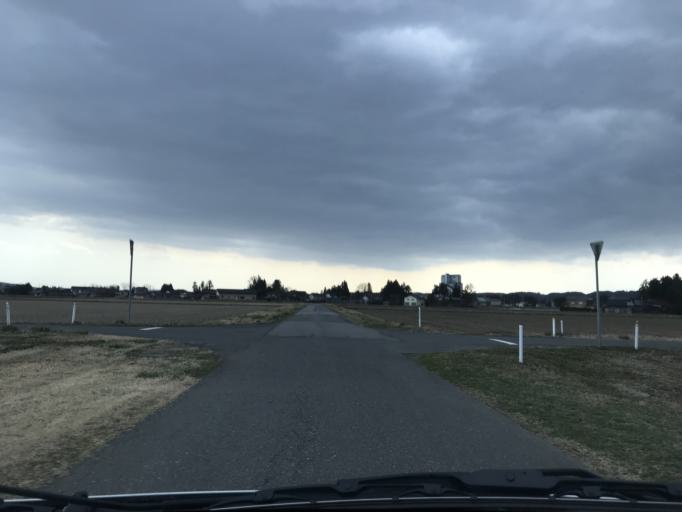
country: JP
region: Iwate
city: Mizusawa
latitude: 39.0726
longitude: 141.1539
